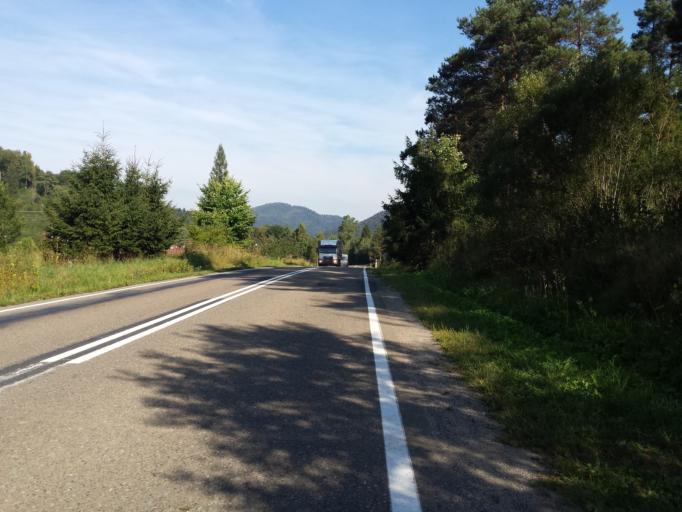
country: PL
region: Subcarpathian Voivodeship
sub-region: Powiat leski
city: Baligrod
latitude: 49.2715
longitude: 22.2889
